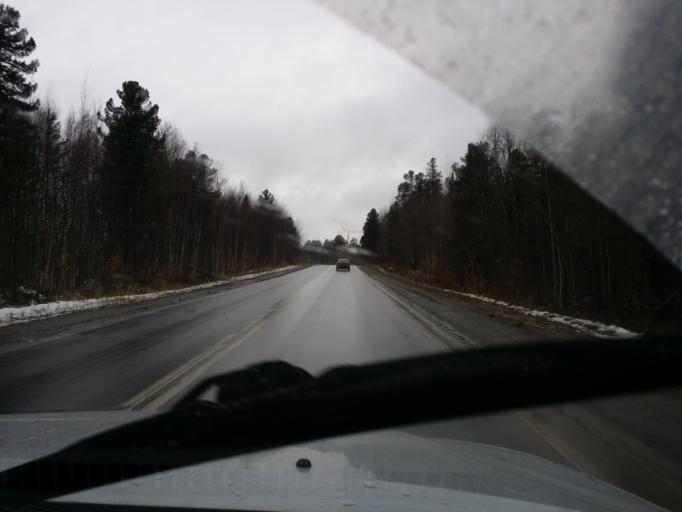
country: RU
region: Khanty-Mansiyskiy Avtonomnyy Okrug
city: Megion
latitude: 61.1629
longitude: 75.6969
